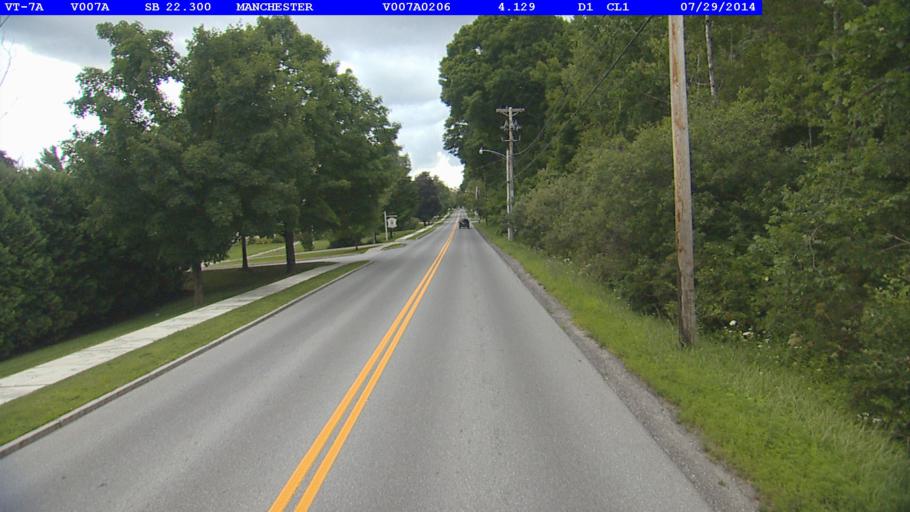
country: US
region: Vermont
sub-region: Bennington County
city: Manchester Center
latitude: 43.1689
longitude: -73.0667
